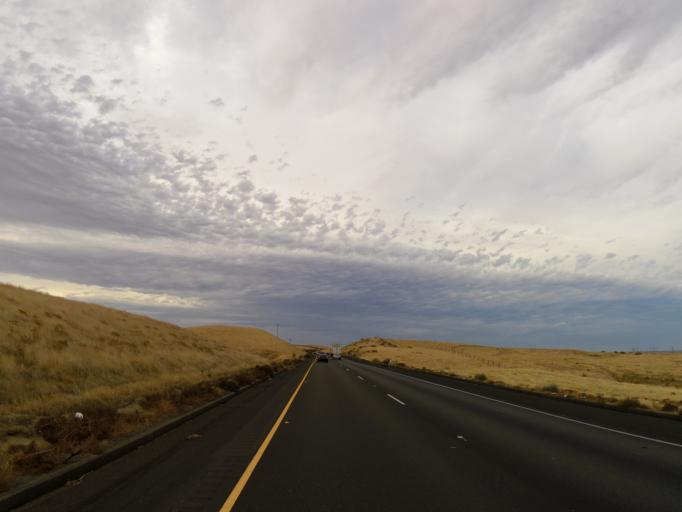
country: US
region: California
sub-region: Kings County
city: Kettleman City
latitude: 36.0018
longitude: -119.9794
